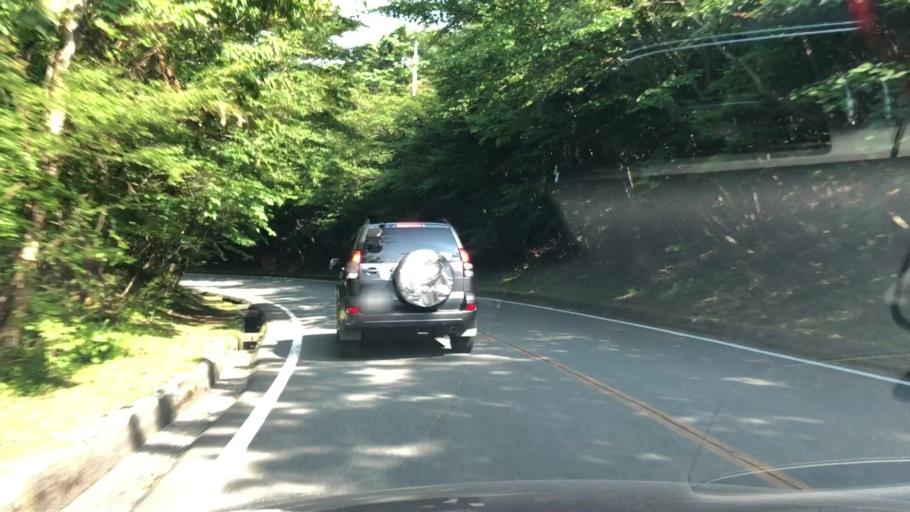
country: JP
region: Shizuoka
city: Gotemba
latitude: 35.3328
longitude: 138.8192
